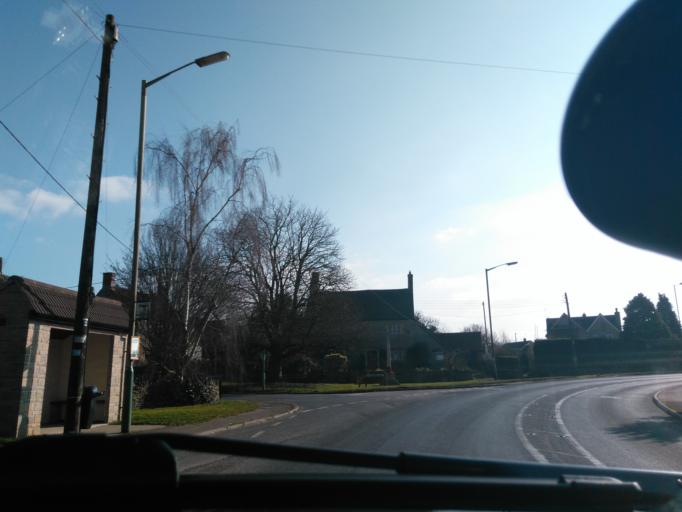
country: GB
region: England
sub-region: Wiltshire
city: Malmesbury
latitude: 51.5546
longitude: -2.1097
